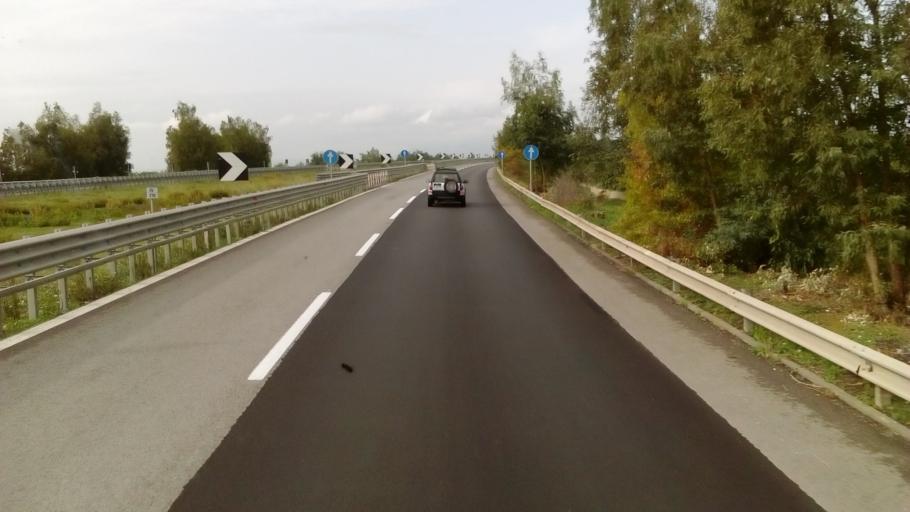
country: IT
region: Sicily
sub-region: Catania
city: Paterno
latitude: 37.4680
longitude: 14.8694
